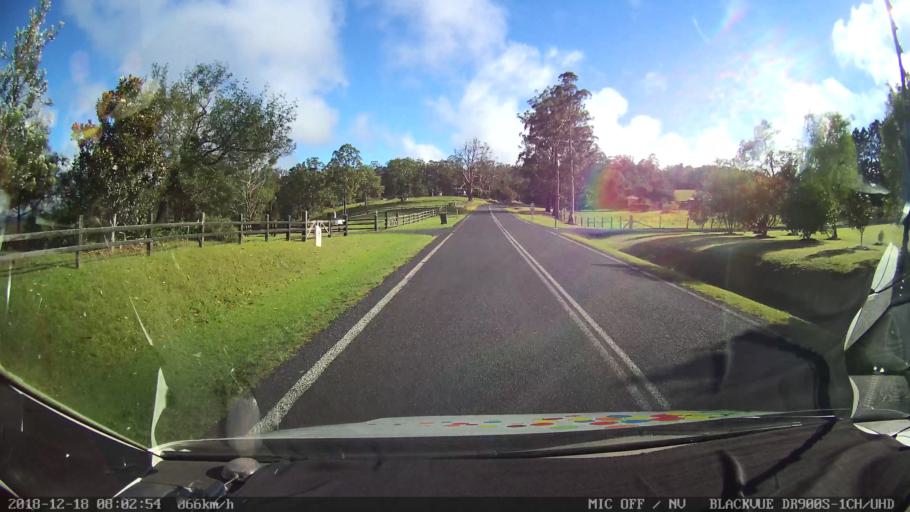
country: AU
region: New South Wales
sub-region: Kyogle
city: Kyogle
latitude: -28.3897
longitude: 152.6366
